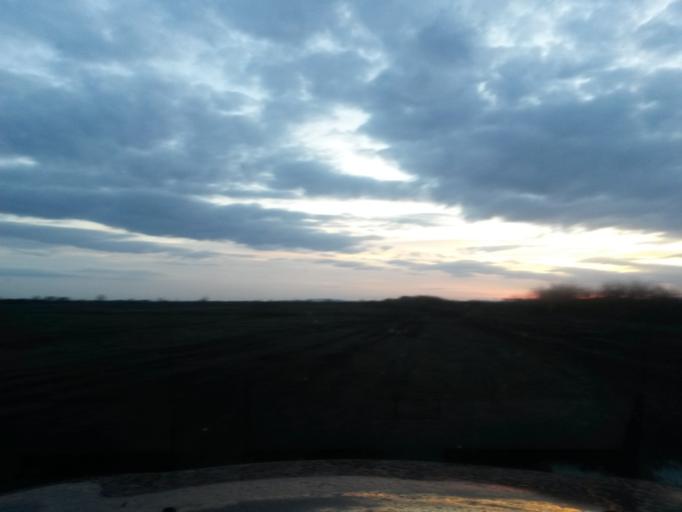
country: SK
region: Kosicky
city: Sobrance
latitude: 48.6984
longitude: 22.0577
